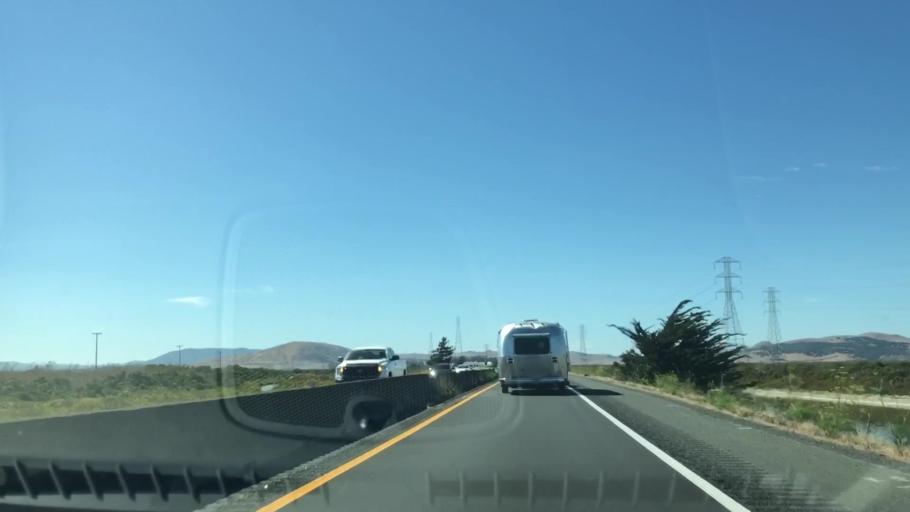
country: US
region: California
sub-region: Marin County
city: Black Point-Green Point
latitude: 38.1529
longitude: -122.3902
